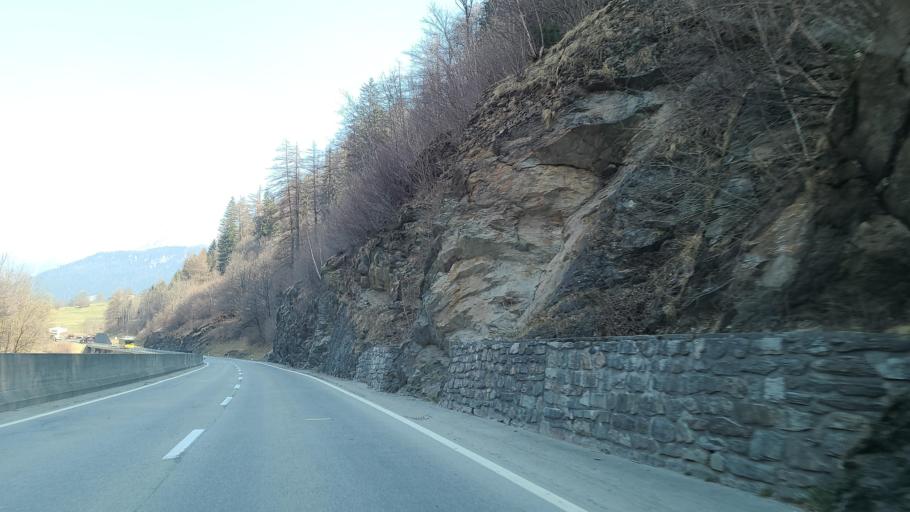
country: CH
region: Grisons
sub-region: Bernina District
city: Poschiavo
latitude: 46.3332
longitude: 10.0602
